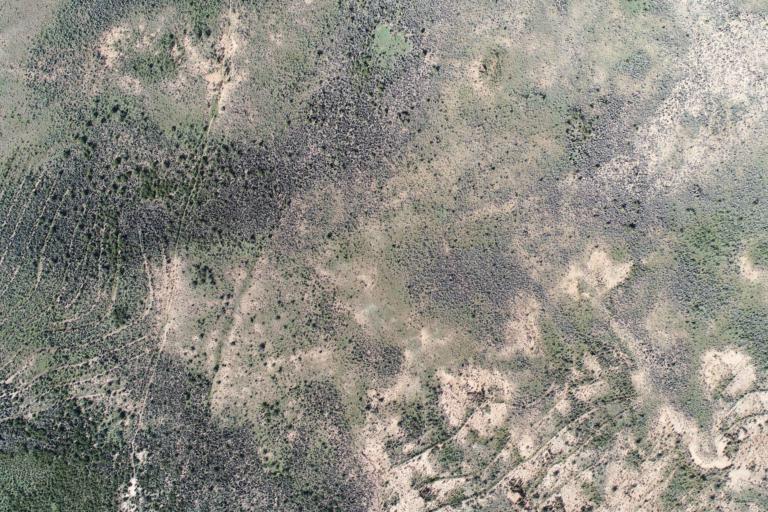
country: BO
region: La Paz
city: Curahuara de Carangas
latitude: -17.3021
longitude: -68.5077
